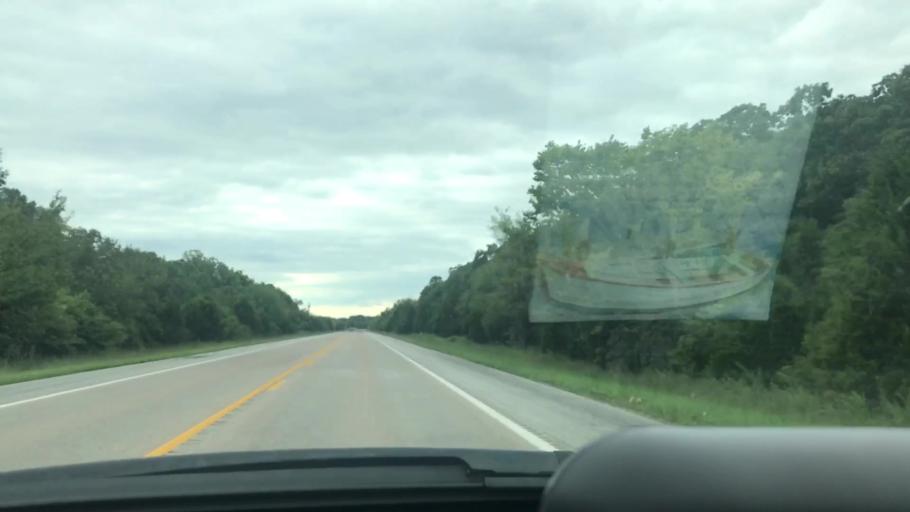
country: US
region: Missouri
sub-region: Benton County
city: Warsaw
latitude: 38.2091
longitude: -93.3329
